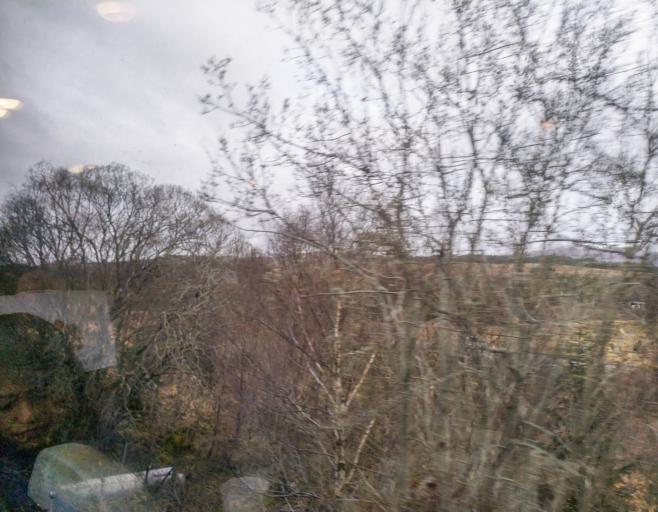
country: GB
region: Scotland
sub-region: Highland
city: Spean Bridge
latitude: 56.8815
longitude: -4.9595
